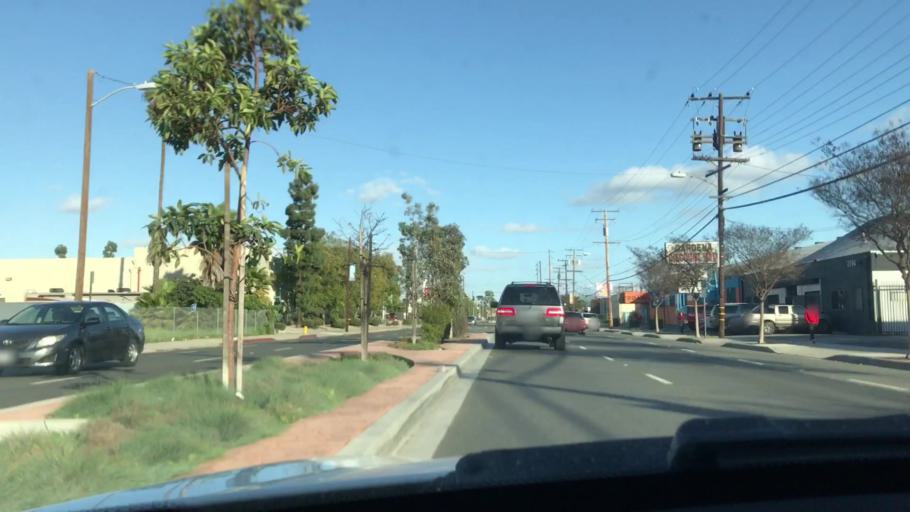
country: US
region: California
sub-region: Los Angeles County
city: Gardena
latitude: 33.9019
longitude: -118.3161
